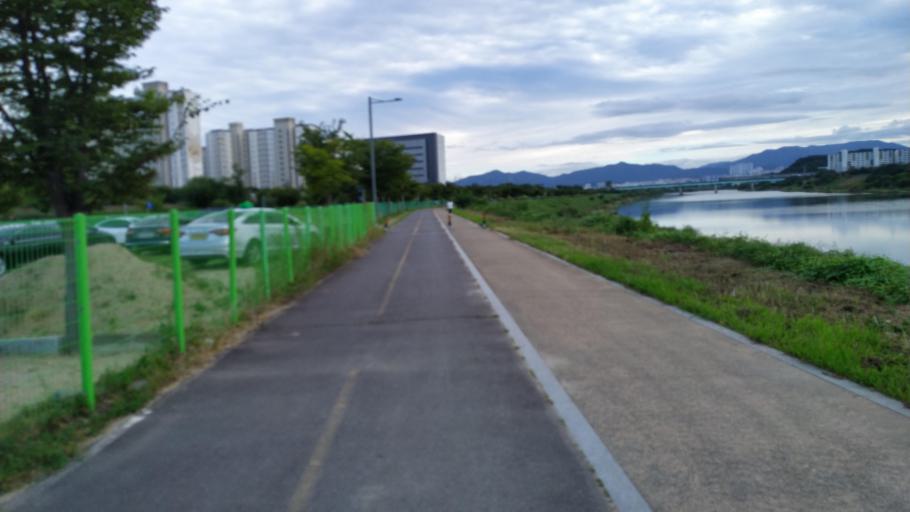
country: KR
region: Daegu
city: Daegu
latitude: 35.9274
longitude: 128.6316
